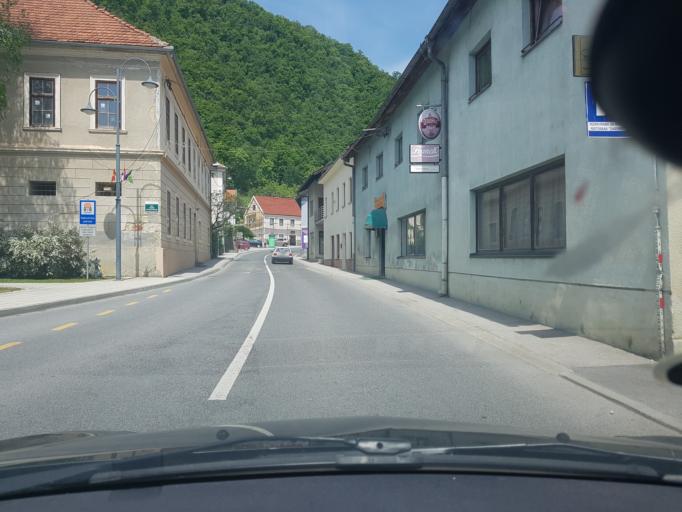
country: HR
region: Krapinsko-Zagorska
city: Pregrada
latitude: 46.1651
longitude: 15.7506
